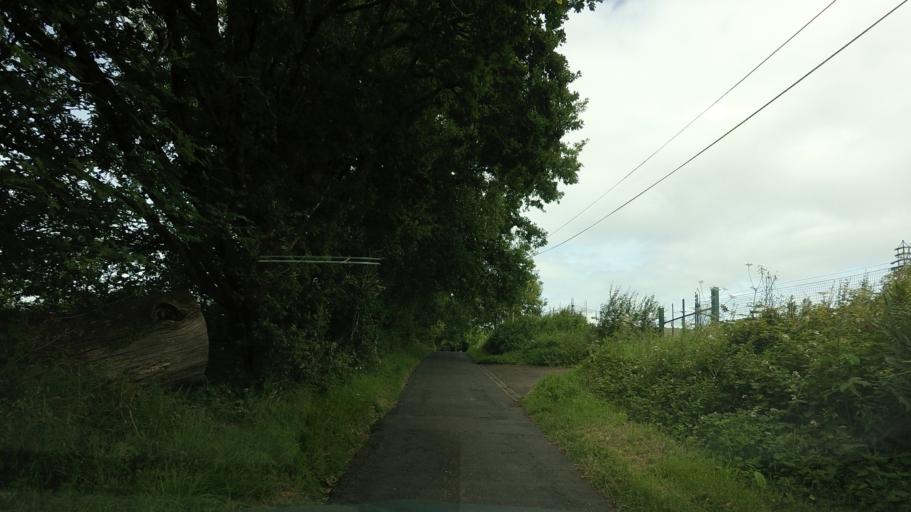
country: GB
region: Scotland
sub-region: Stirling
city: Killearn
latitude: 56.0769
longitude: -4.4500
